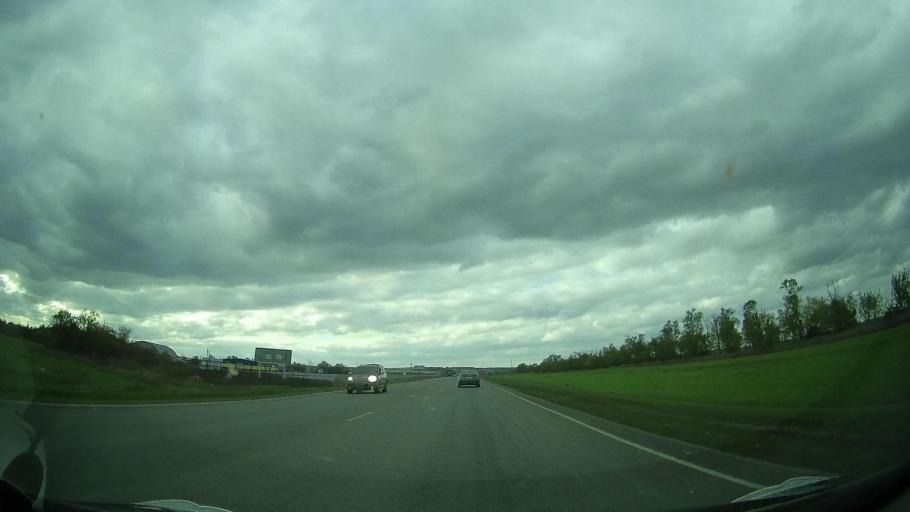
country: RU
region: Rostov
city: Kagal'nitskaya
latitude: 46.8719
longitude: 40.1656
